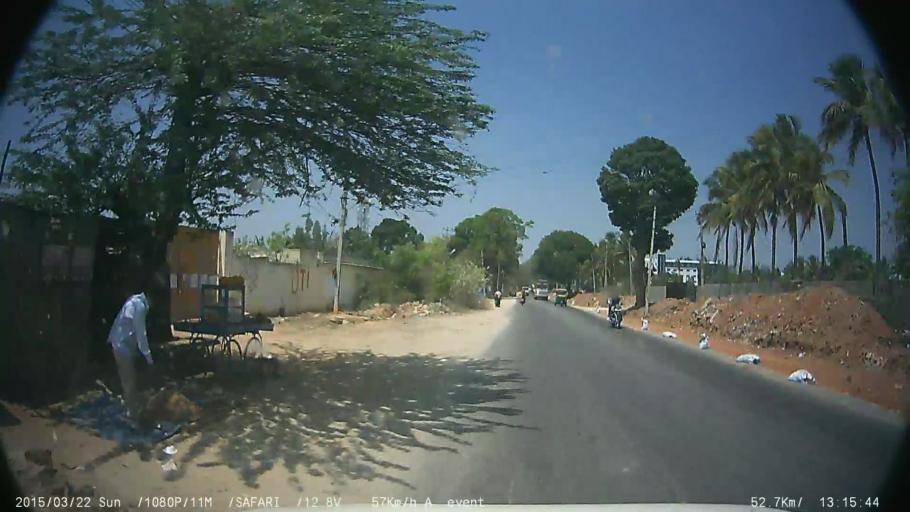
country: IN
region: Karnataka
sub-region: Bangalore Urban
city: Bangalore
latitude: 12.8254
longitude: 77.5861
